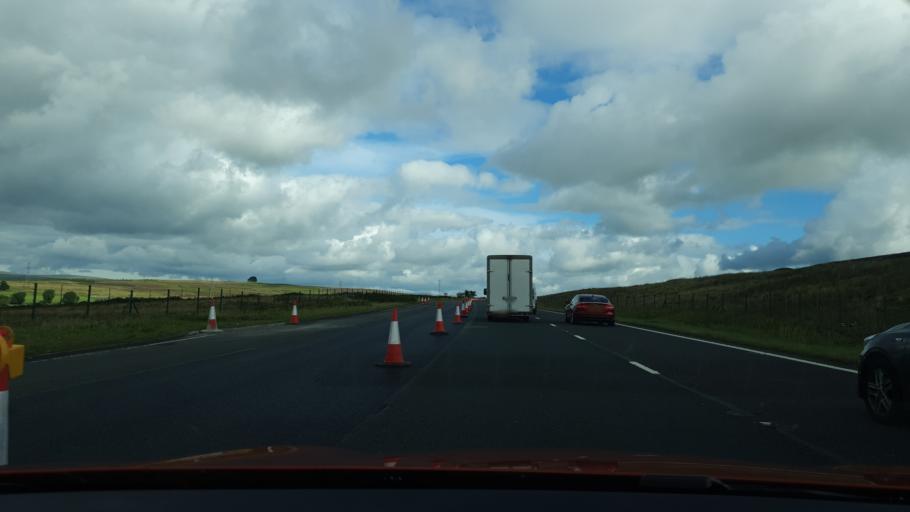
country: GB
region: England
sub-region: Cumbria
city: Appleby-in-Westmorland
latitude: 54.4858
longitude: -2.6383
